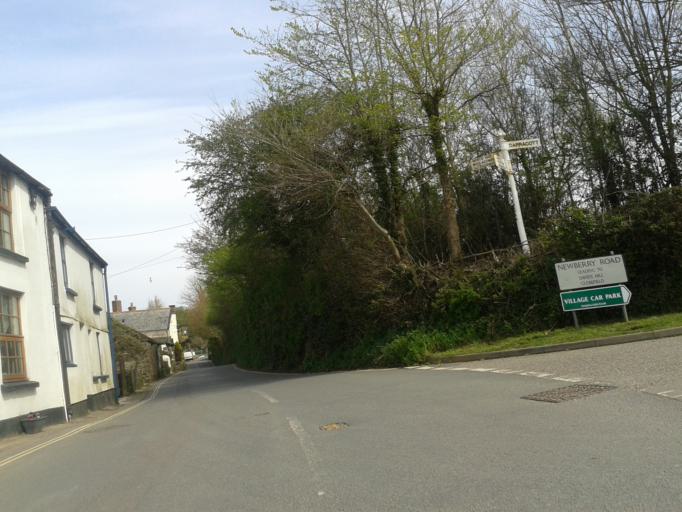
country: GB
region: England
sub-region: Devon
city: Braunton
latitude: 51.1365
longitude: -4.1961
